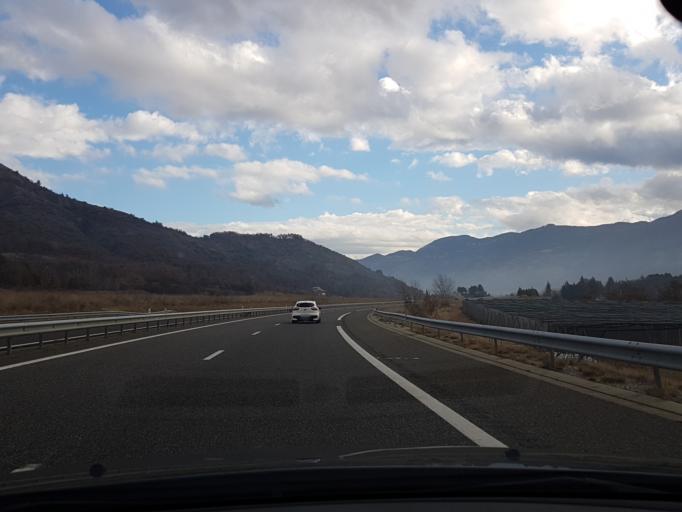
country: FR
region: Provence-Alpes-Cote d'Azur
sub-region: Departement des Hautes-Alpes
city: Tallard
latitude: 44.4176
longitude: 5.9713
